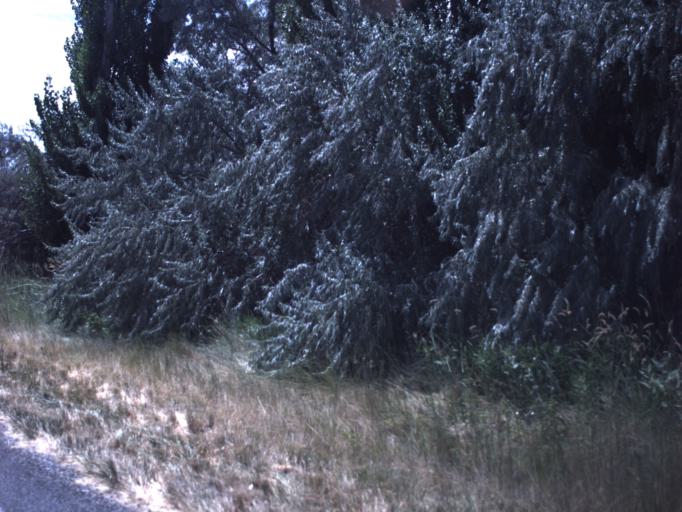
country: US
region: Utah
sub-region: Box Elder County
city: Tremonton
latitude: 41.6575
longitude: -112.2961
